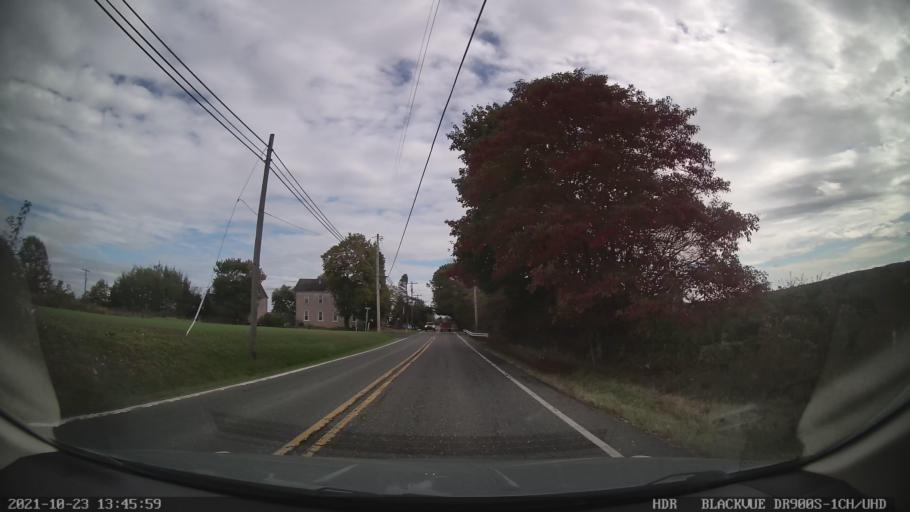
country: US
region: Pennsylvania
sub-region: Montgomery County
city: Pennsburg
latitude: 40.3778
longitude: -75.5207
